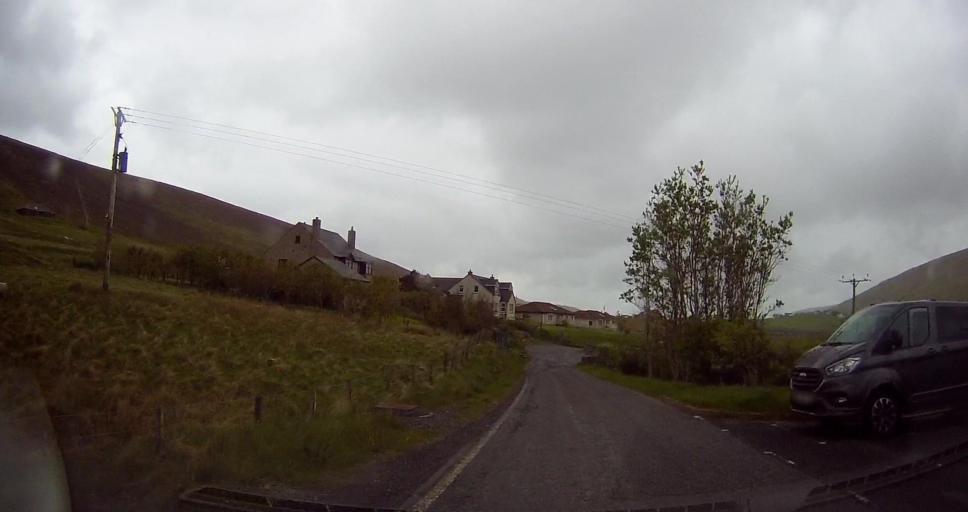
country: GB
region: Scotland
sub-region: Shetland Islands
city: Lerwick
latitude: 60.2554
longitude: -1.2895
